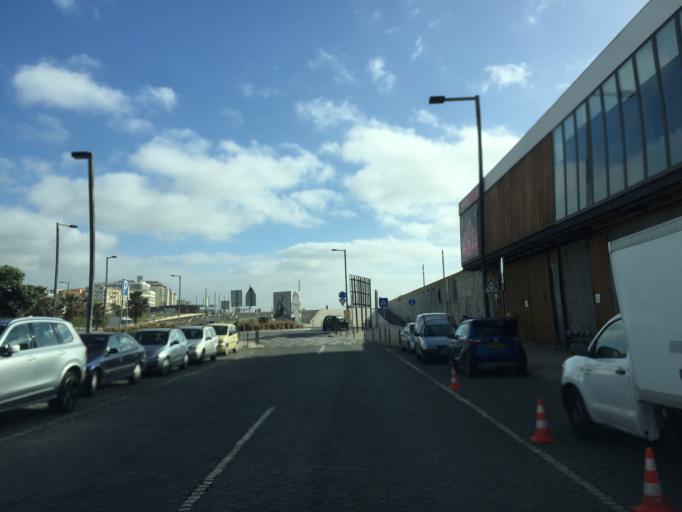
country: PT
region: Setubal
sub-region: Almada
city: Costa de Caparica
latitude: 38.6445
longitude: -9.2409
